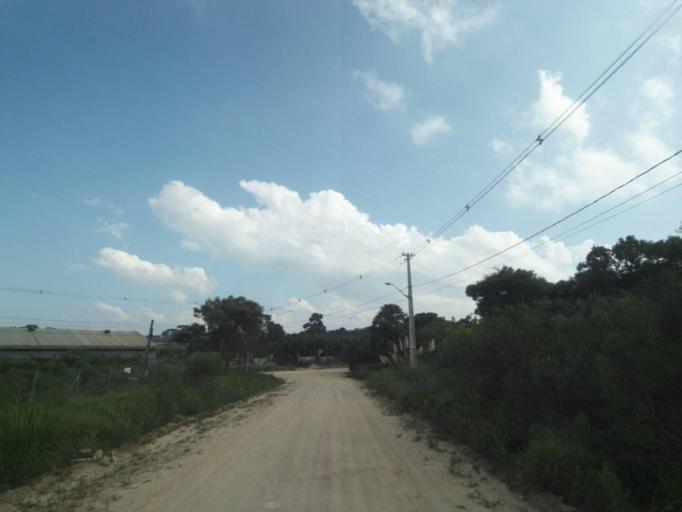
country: BR
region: Parana
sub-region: Araucaria
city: Araucaria
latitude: -25.5131
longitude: -49.3426
